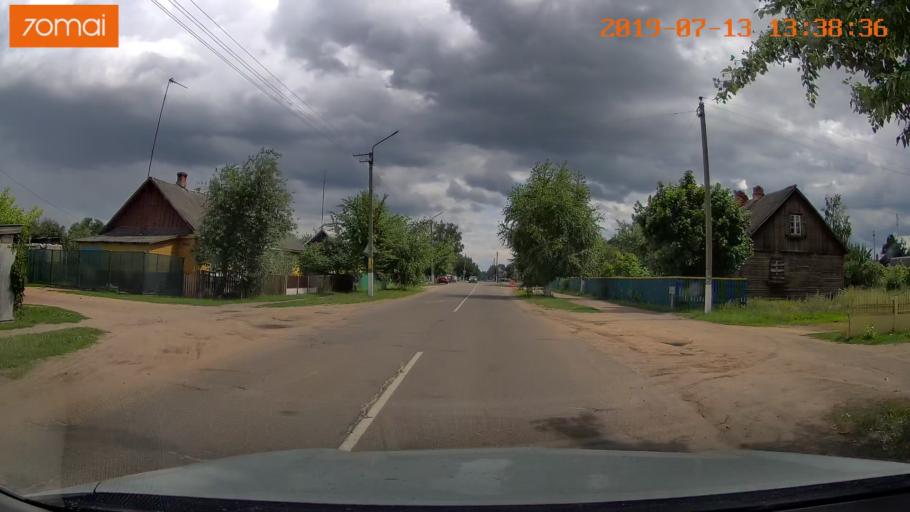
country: BY
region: Mogilev
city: Asipovichy
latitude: 53.2977
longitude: 28.6358
